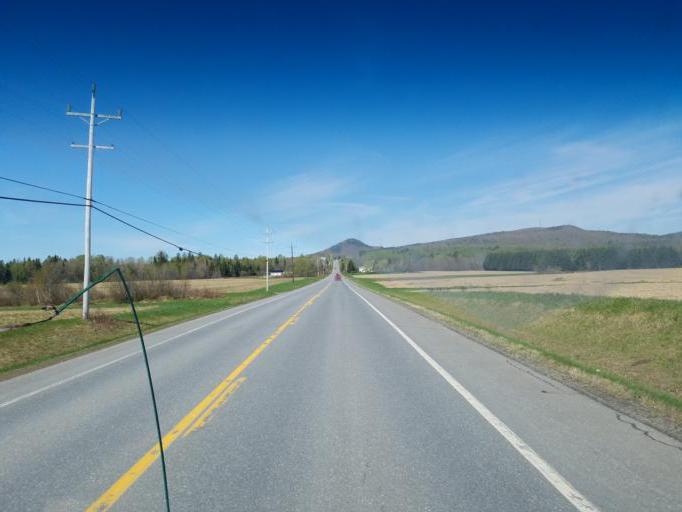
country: US
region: Maine
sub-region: Aroostook County
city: Presque Isle
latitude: 46.6669
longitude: -68.1965
